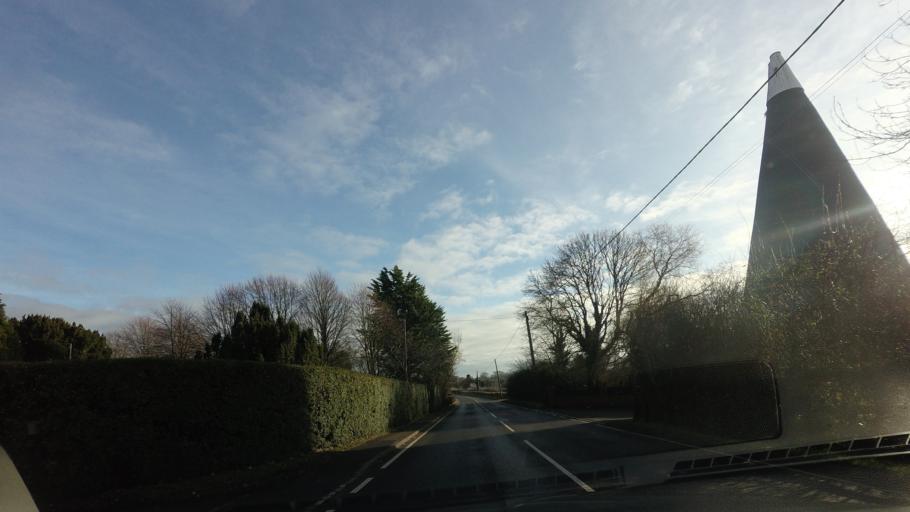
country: GB
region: England
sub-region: East Sussex
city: Bexhill-on-Sea
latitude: 50.8729
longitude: 0.4360
